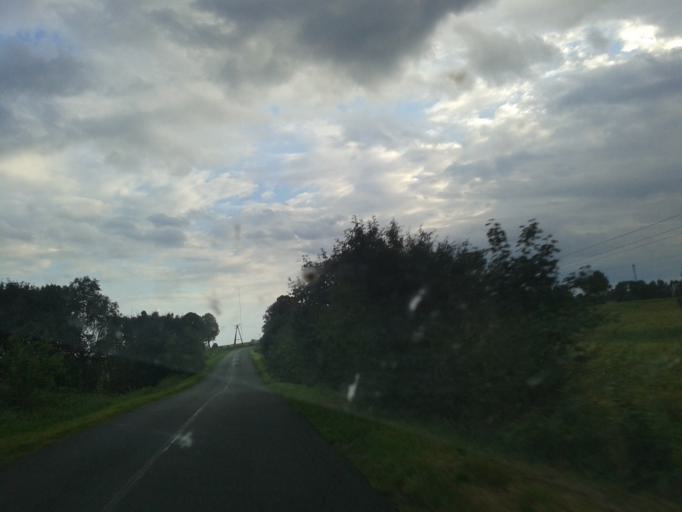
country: PL
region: West Pomeranian Voivodeship
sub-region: Powiat koszalinski
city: Bobolice
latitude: 53.8908
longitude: 16.5179
